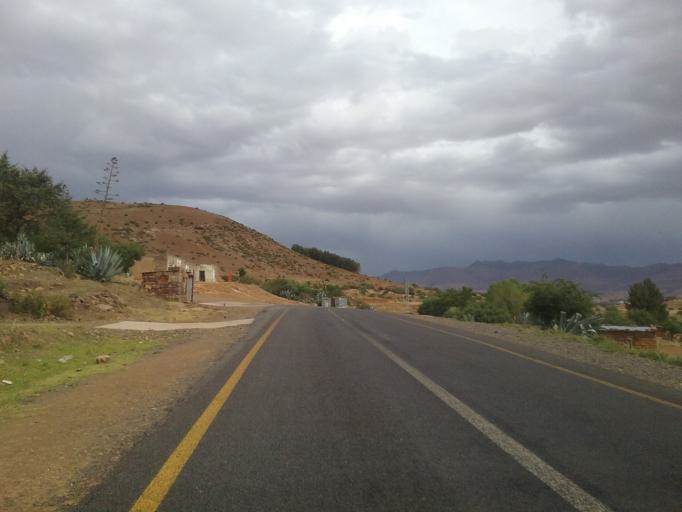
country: LS
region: Quthing
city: Quthing
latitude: -30.3752
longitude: 27.7046
